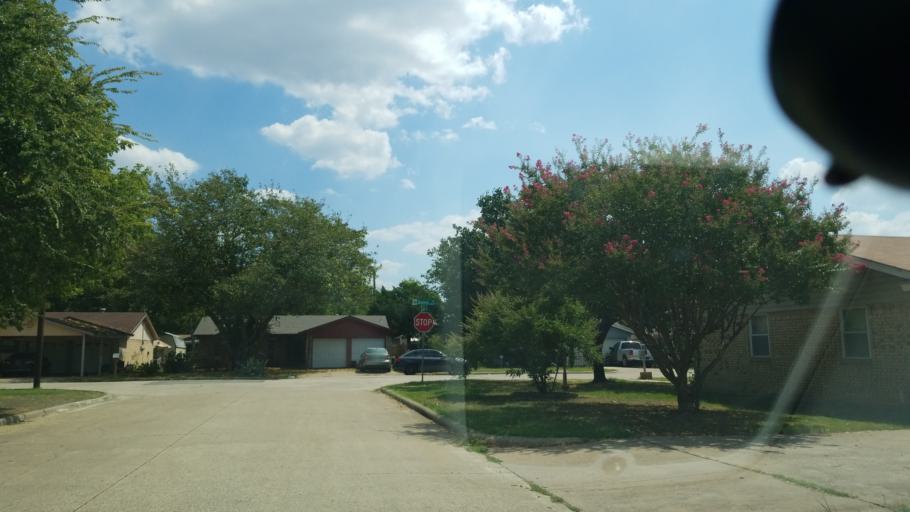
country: US
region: Texas
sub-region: Dallas County
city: Grand Prairie
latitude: 32.7091
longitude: -96.9872
